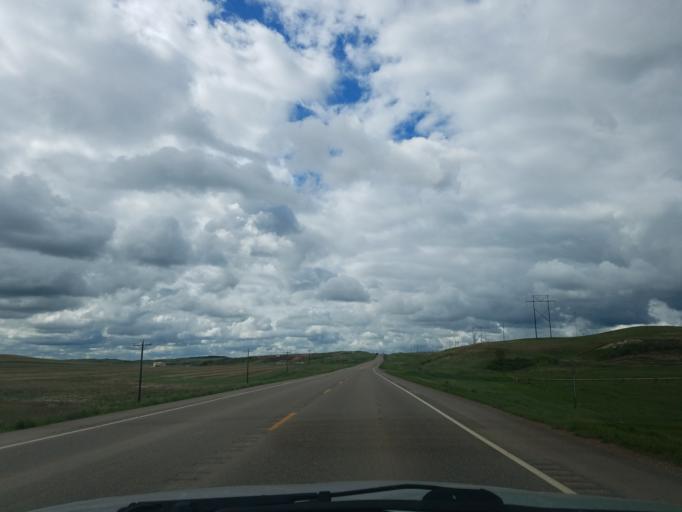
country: US
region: North Dakota
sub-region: McKenzie County
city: Watford City
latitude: 47.7016
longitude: -103.2835
